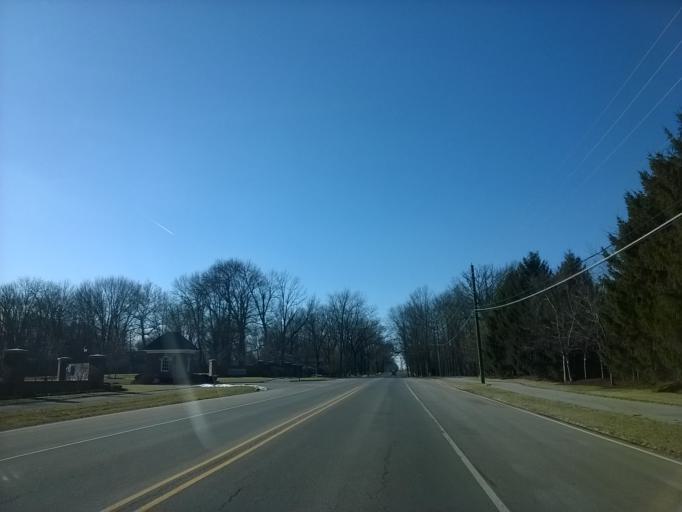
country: US
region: Indiana
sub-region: Boone County
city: Zionsville
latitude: 39.9412
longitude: -86.2114
